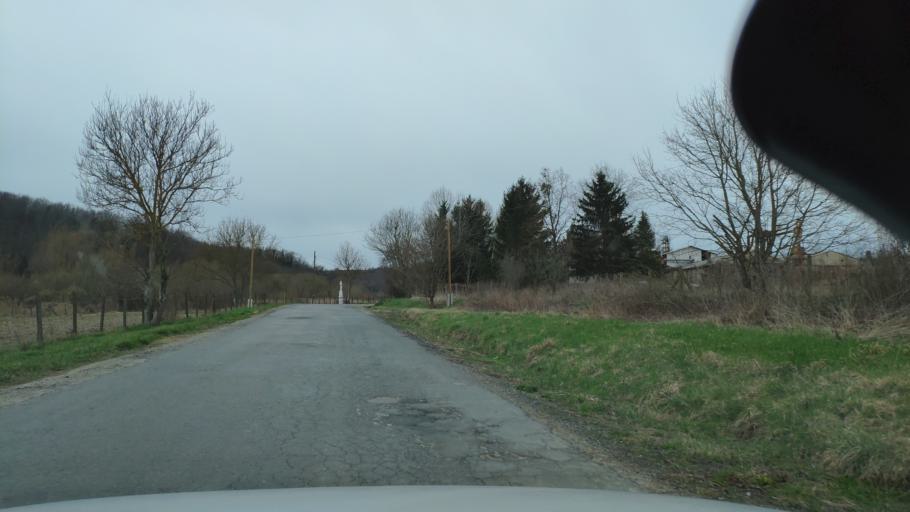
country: HU
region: Zala
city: Pacsa
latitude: 46.6743
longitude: 17.0696
